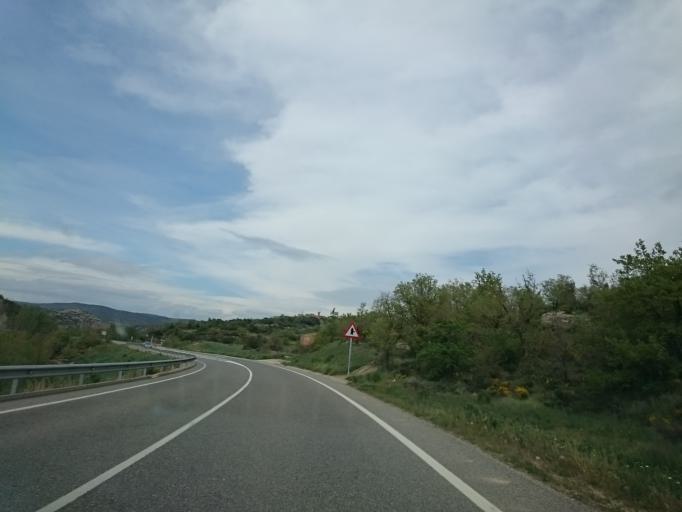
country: ES
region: Catalonia
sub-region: Provincia de Lleida
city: Tora de Riubregos
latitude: 41.8132
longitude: 1.3207
